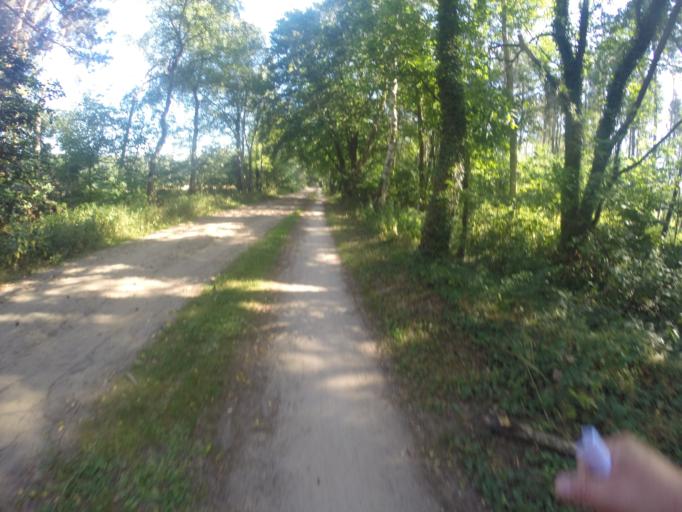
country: NL
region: Gelderland
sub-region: Gemeente Lochem
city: Almen
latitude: 52.1254
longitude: 6.3284
